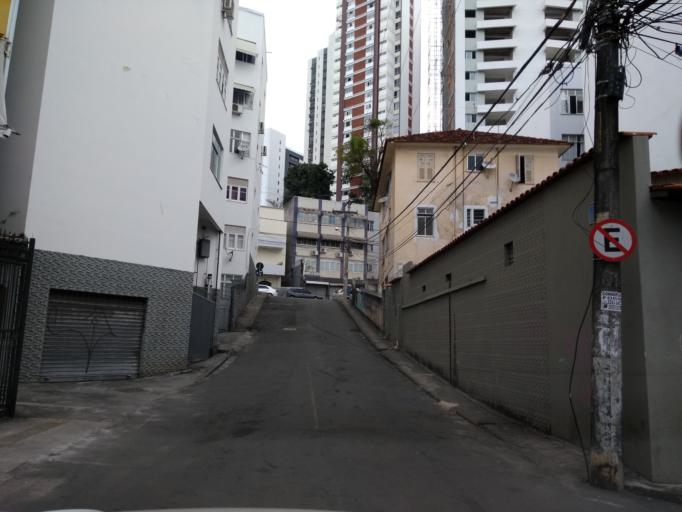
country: BR
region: Bahia
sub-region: Salvador
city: Salvador
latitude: -13.0016
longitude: -38.5273
